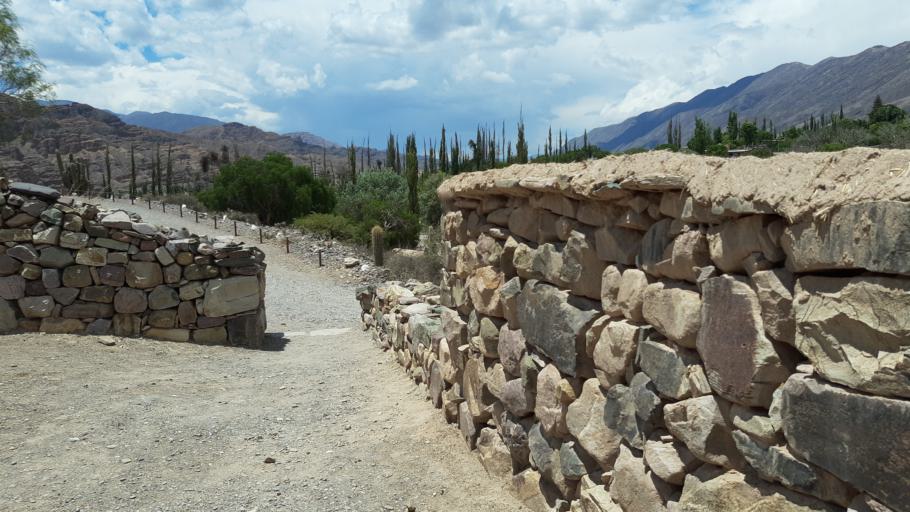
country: AR
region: Jujuy
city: Maimara
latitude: -23.5854
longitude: -65.4004
